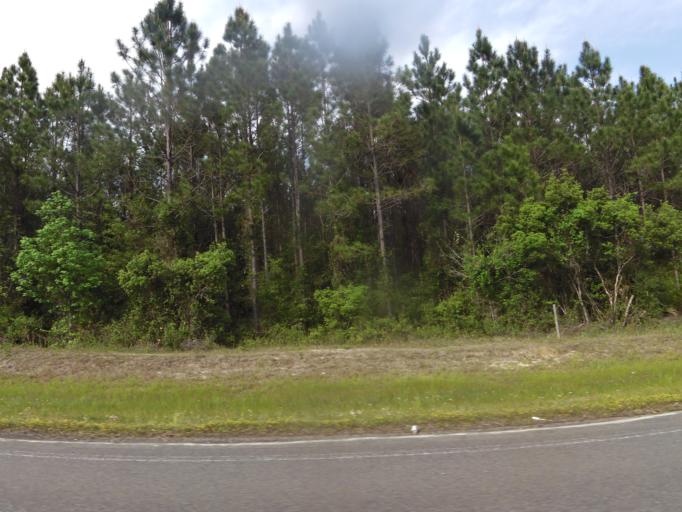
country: US
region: Georgia
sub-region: Camden County
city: Kingsland
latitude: 30.6965
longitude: -81.7427
